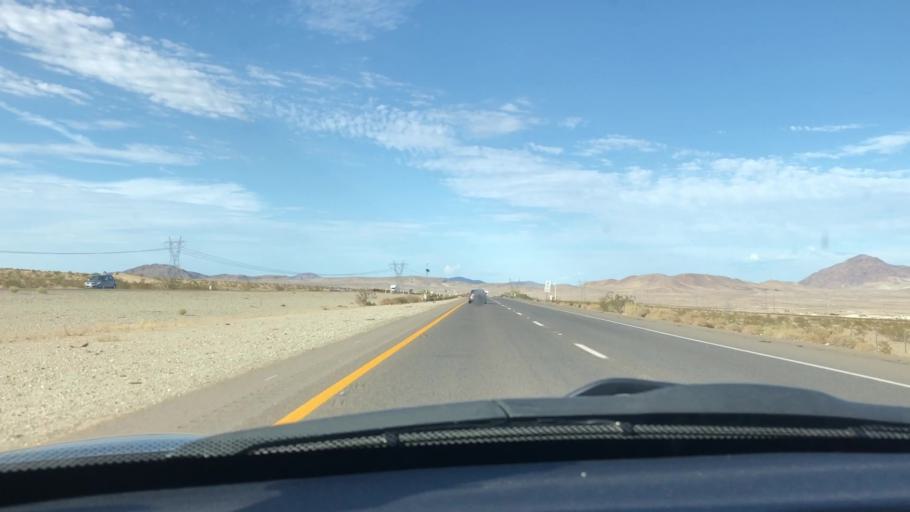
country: US
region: California
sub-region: San Bernardino County
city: Fort Irwin
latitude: 35.0423
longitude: -116.4557
